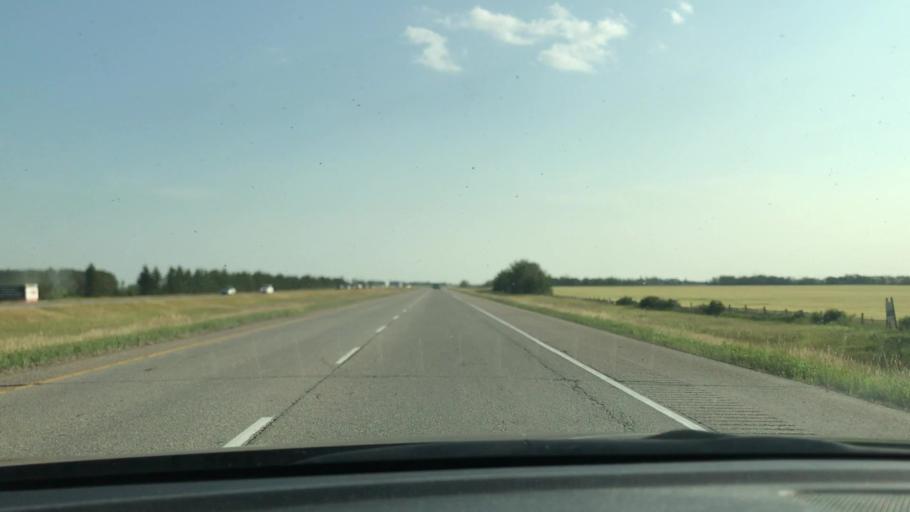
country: CA
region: Alberta
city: Leduc
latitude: 53.2143
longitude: -113.5861
